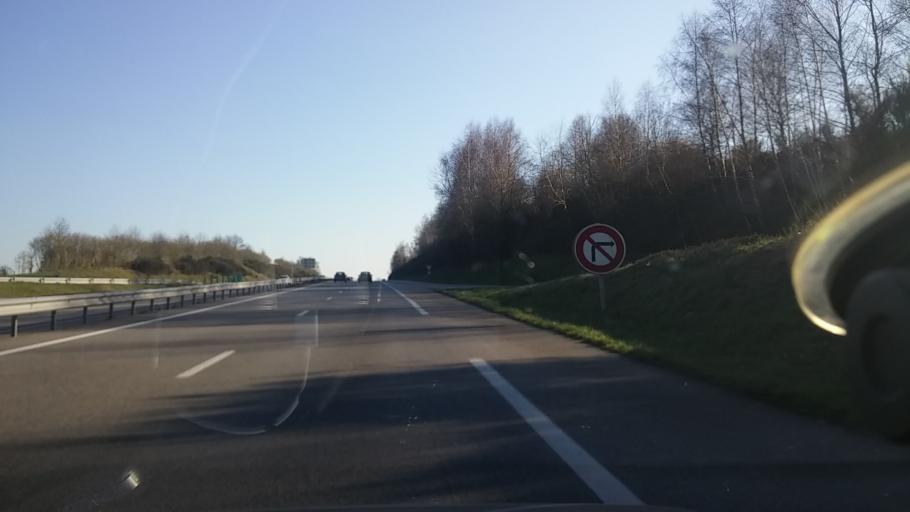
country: FR
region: Limousin
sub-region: Departement de la Haute-Vienne
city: Saint-Sulpice-les-Feuilles
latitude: 46.3543
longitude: 1.4268
